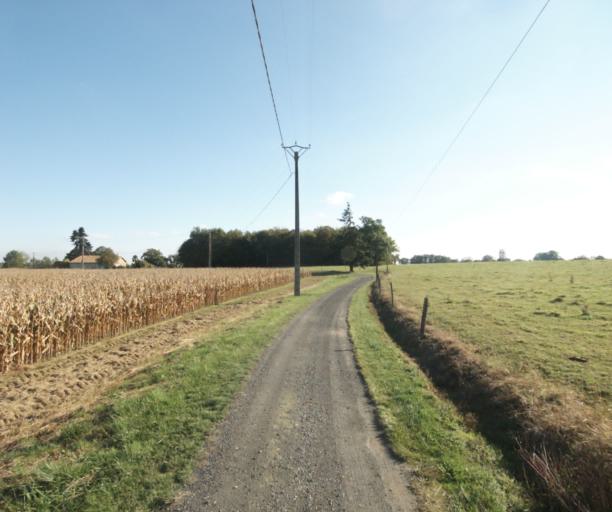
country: FR
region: Midi-Pyrenees
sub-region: Departement du Gers
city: Eauze
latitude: 43.7915
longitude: 0.1491
